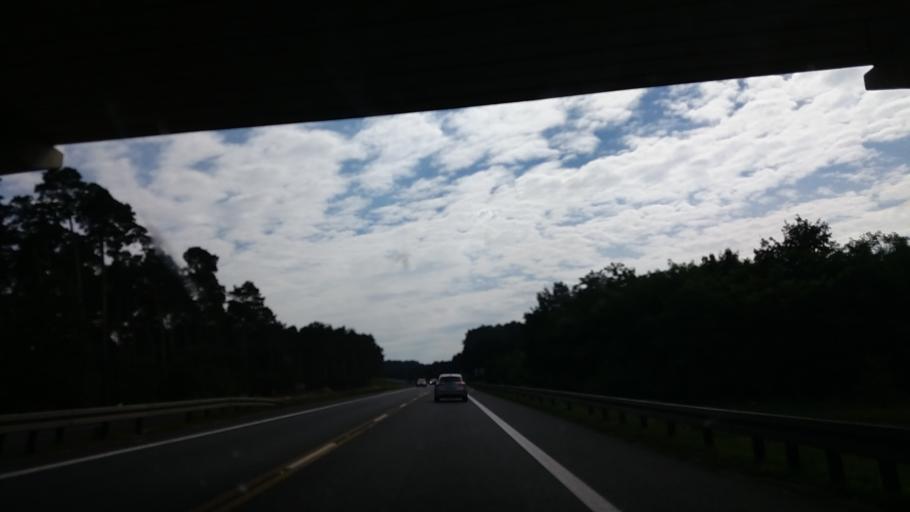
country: PL
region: Lubusz
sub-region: Zielona Gora
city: Zielona Gora
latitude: 51.9887
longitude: 15.5709
